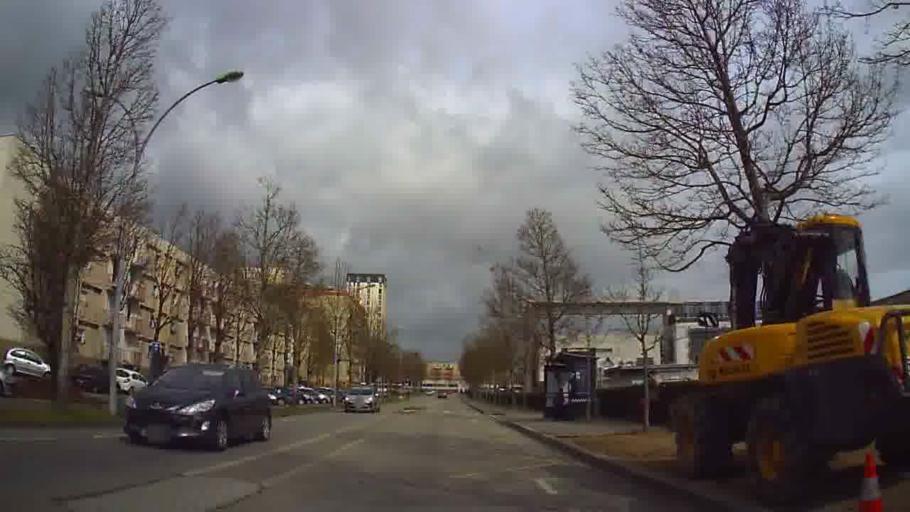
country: FR
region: Brittany
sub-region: Departement d'Ille-et-Vilaine
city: Rennes
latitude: 48.1190
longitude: -1.7046
